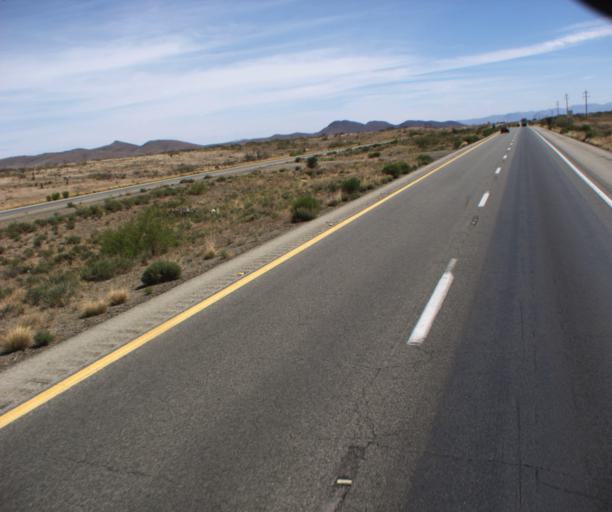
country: US
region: Arizona
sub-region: Cochise County
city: Willcox
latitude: 32.3601
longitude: -109.6686
